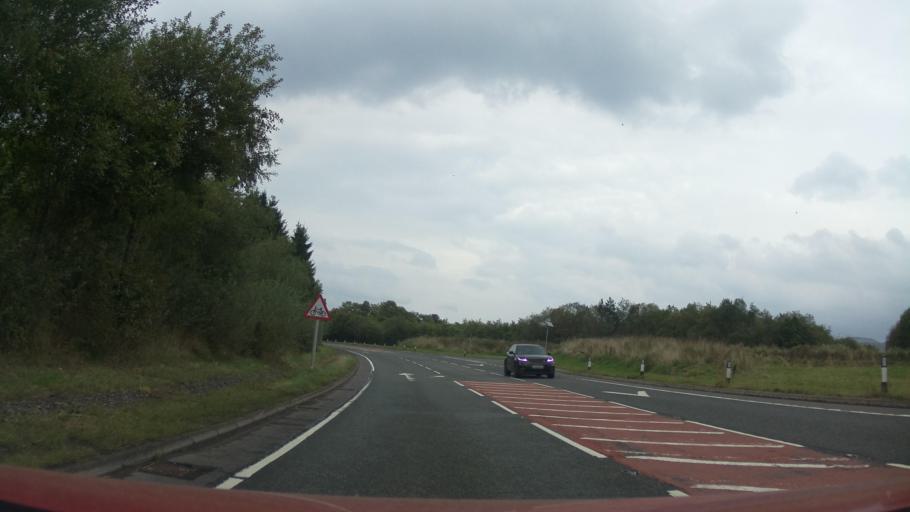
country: GB
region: Scotland
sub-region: Dumfries and Galloway
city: Moffat
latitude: 55.2924
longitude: -3.4456
